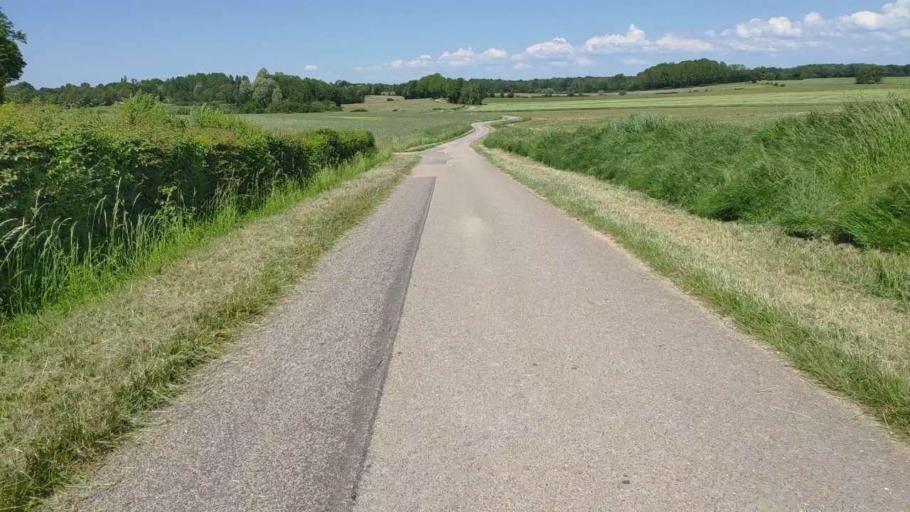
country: FR
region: Franche-Comte
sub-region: Departement du Jura
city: Bletterans
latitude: 46.7472
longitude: 5.3712
